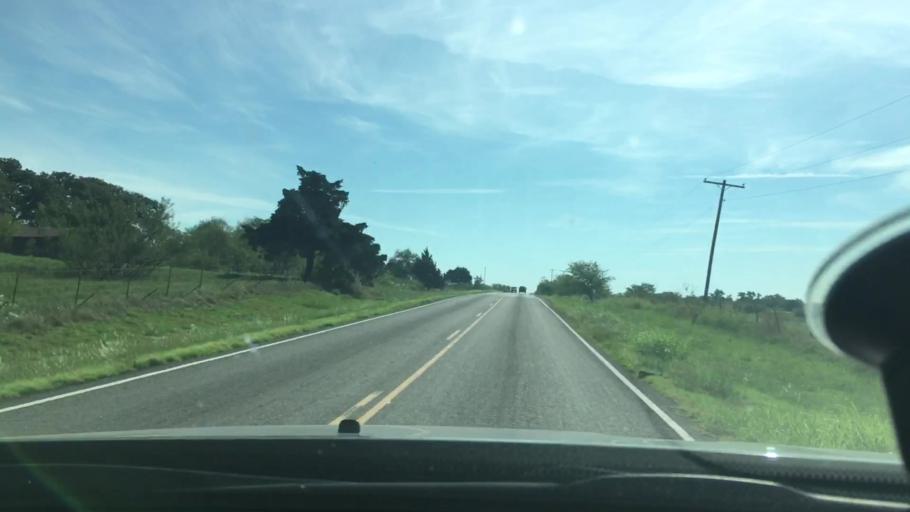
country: US
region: Oklahoma
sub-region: Carter County
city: Ardmore
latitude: 34.3327
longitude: -97.1954
